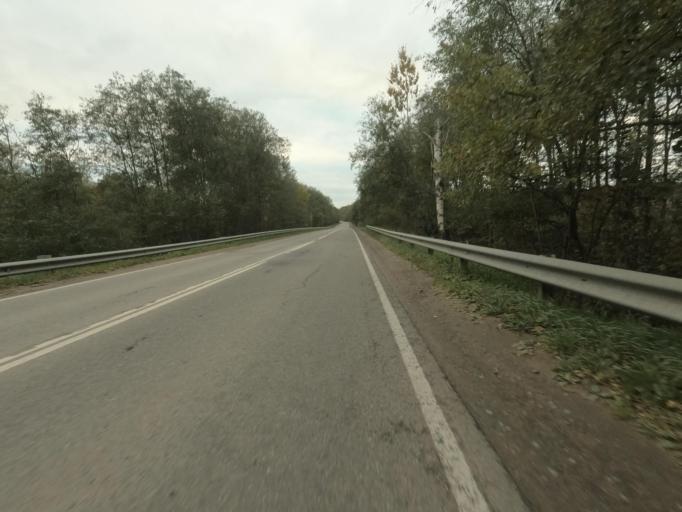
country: RU
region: Leningrad
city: Pavlovo
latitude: 59.7929
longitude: 30.9572
